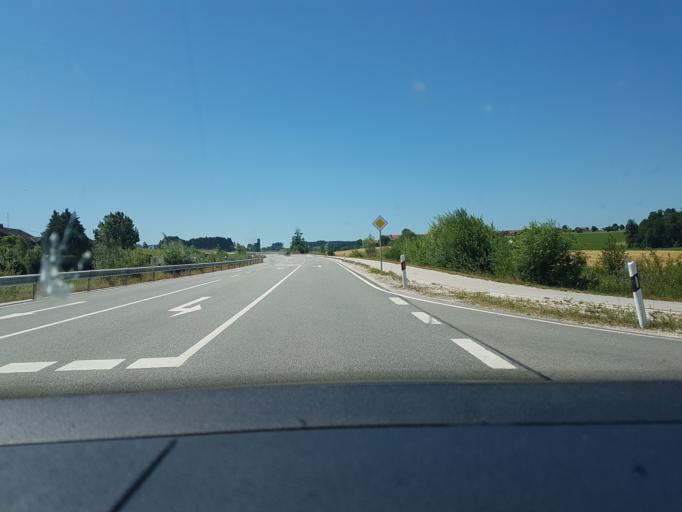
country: DE
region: Bavaria
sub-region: Upper Bavaria
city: Ainring
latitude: 47.8362
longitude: 12.9163
